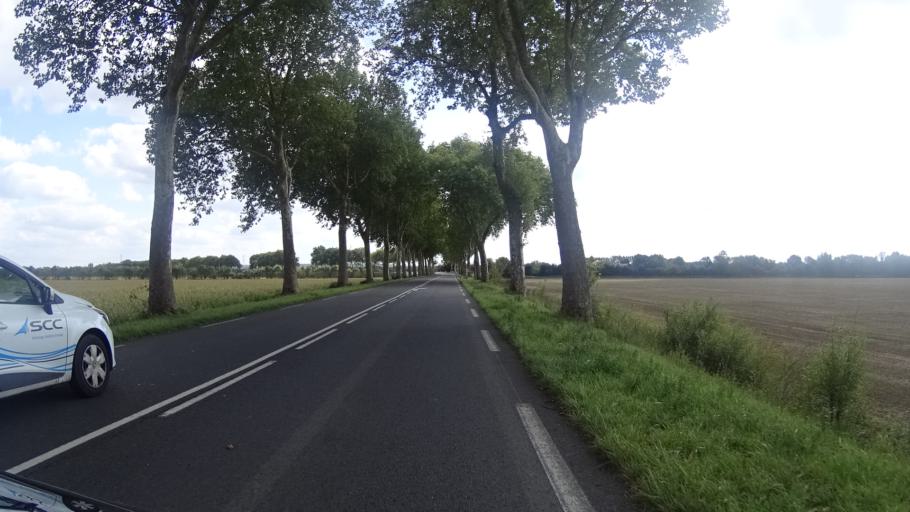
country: FR
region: Pays de la Loire
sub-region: Departement de Maine-et-Loire
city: Trelaze
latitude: 47.4281
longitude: -0.4709
